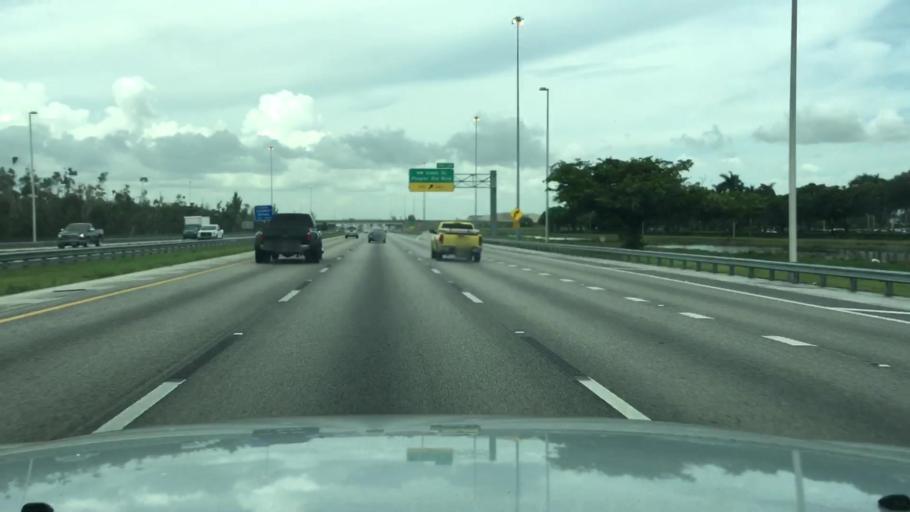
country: US
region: Florida
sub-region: Miami-Dade County
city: Doral
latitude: 25.8602
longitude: -80.3922
